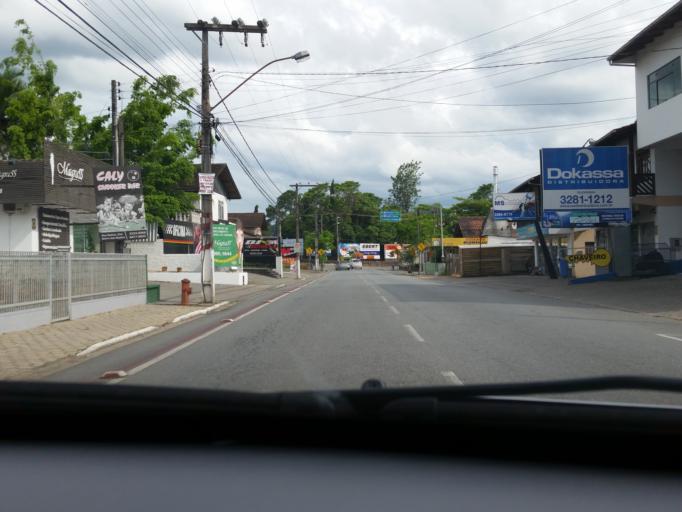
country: BR
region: Santa Catarina
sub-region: Indaial
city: Indaial
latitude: -26.8915
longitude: -49.2429
